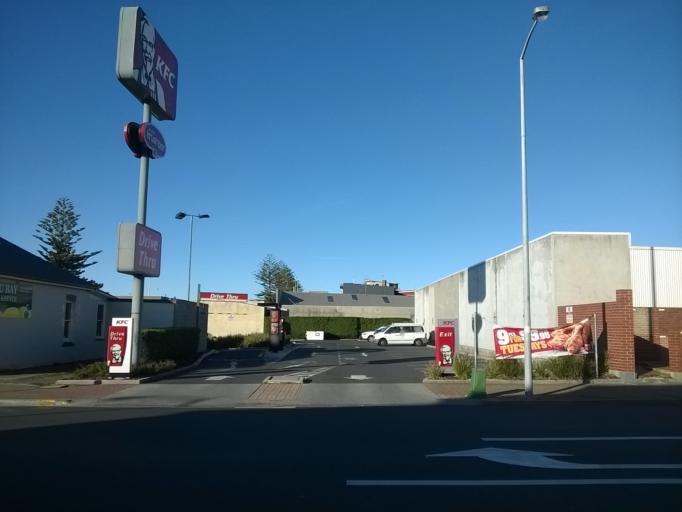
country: AU
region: Tasmania
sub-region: Burnie
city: Burnie
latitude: -41.0497
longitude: 145.9040
